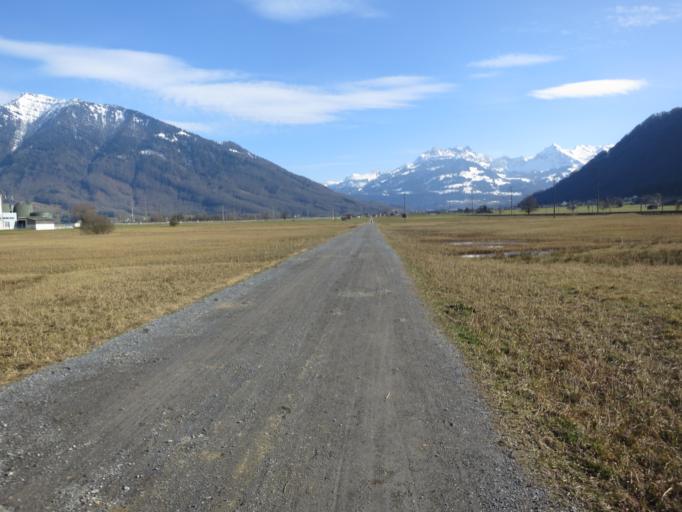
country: CH
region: Glarus
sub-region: Glarus
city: Bilten
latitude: 47.1644
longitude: 9.0077
